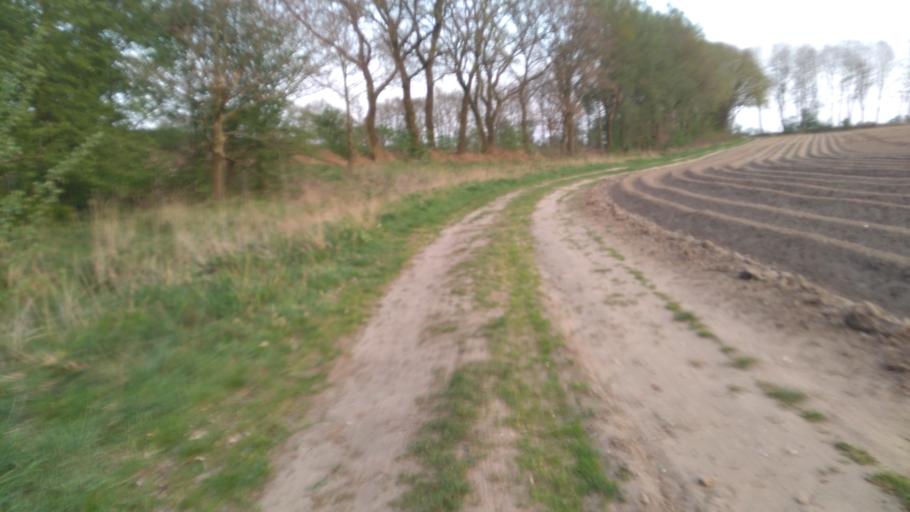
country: DE
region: Lower Saxony
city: Bliedersdorf
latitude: 53.4778
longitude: 9.5474
